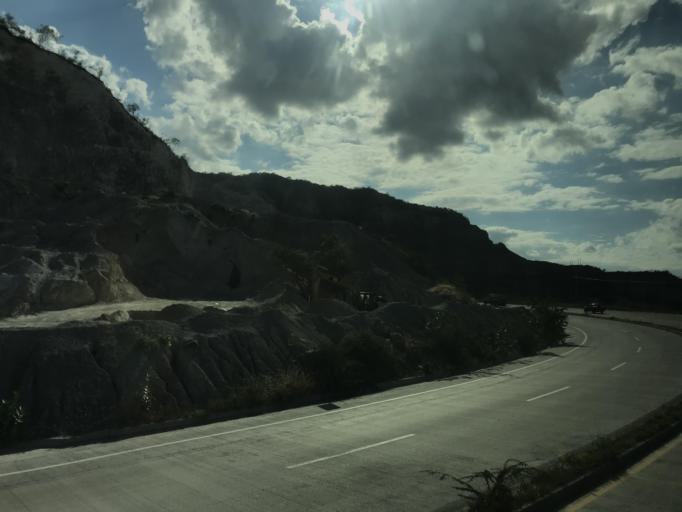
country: GT
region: El Progreso
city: Guastatoya
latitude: 14.8476
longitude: -90.1246
